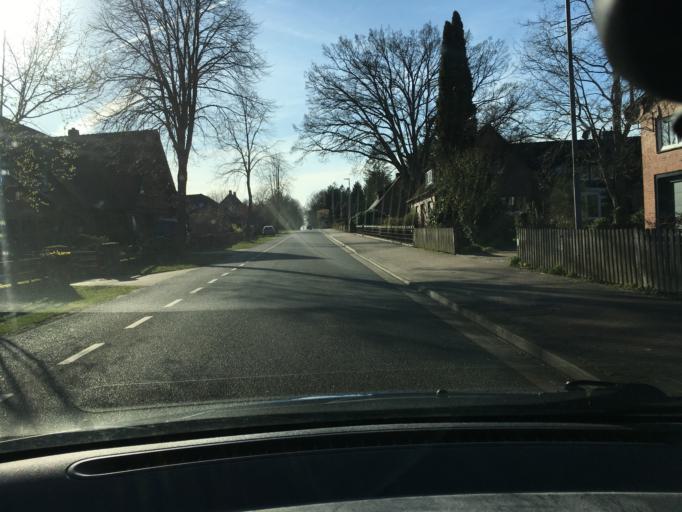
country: DE
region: Lower Saxony
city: Bispingen
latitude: 53.0965
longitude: 10.0211
